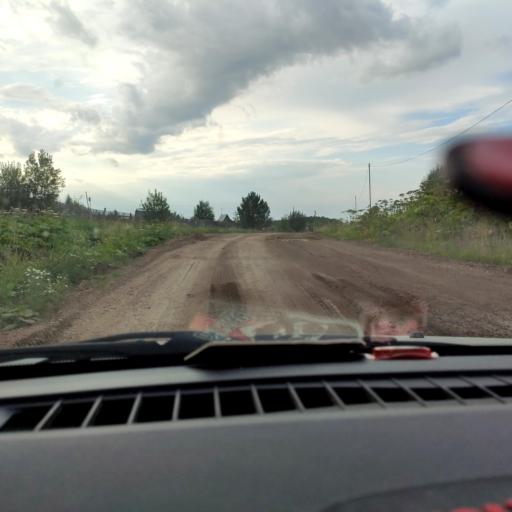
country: RU
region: Perm
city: Kultayevo
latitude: 57.8213
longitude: 55.9989
